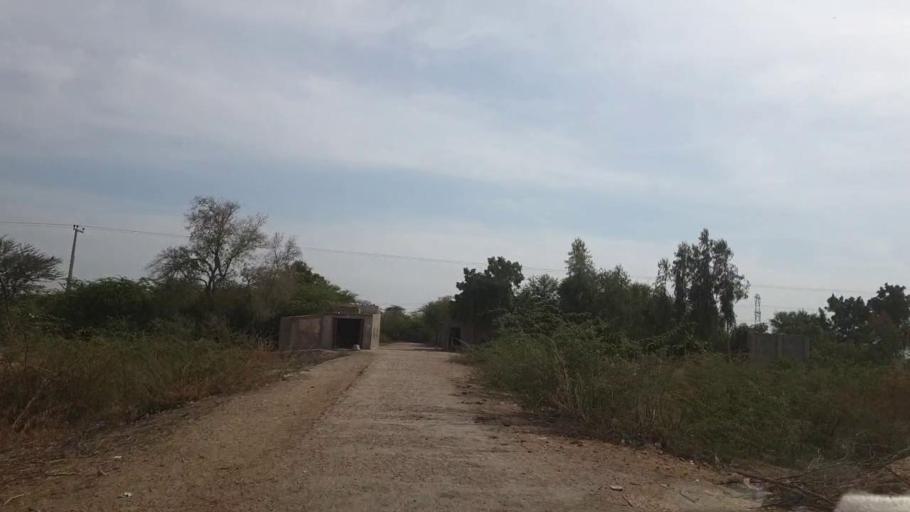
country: PK
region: Sindh
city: Nabisar
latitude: 25.0471
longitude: 69.5709
